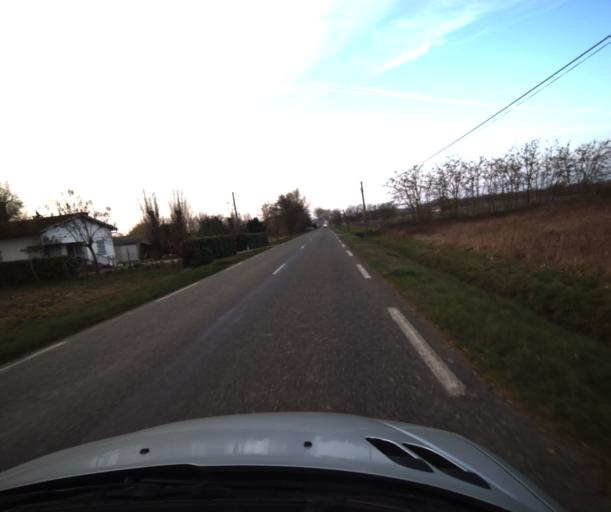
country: FR
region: Midi-Pyrenees
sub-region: Departement de la Haute-Garonne
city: Fronton
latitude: 43.8693
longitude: 1.3807
